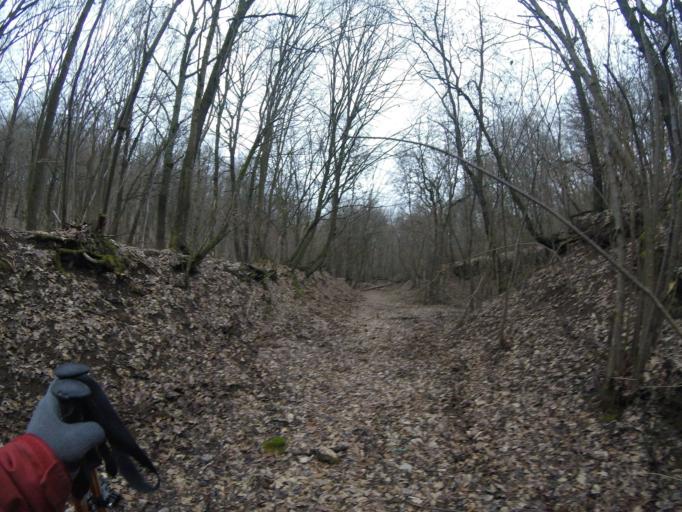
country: HU
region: Borsod-Abauj-Zemplen
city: Rudabanya
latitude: 48.4493
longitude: 20.6087
